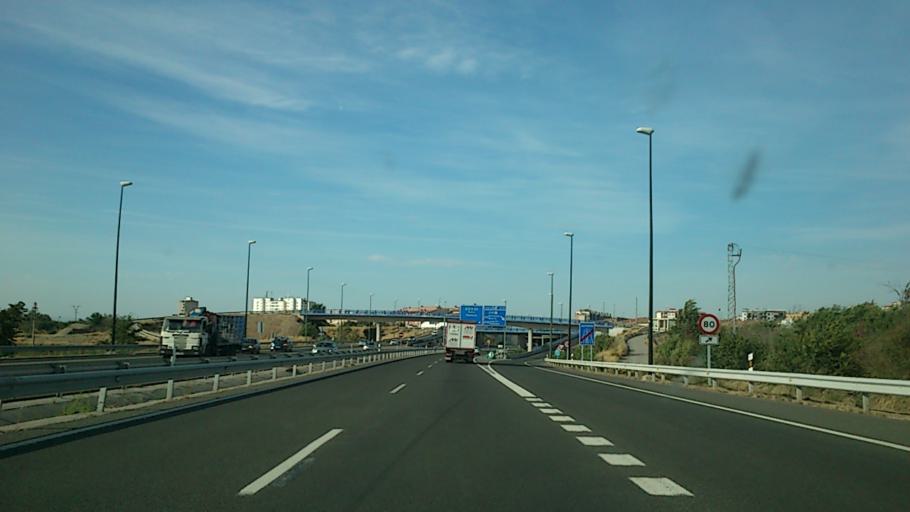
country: ES
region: Aragon
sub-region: Provincia de Zaragoza
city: Zaragoza
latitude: 41.6619
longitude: -0.8394
